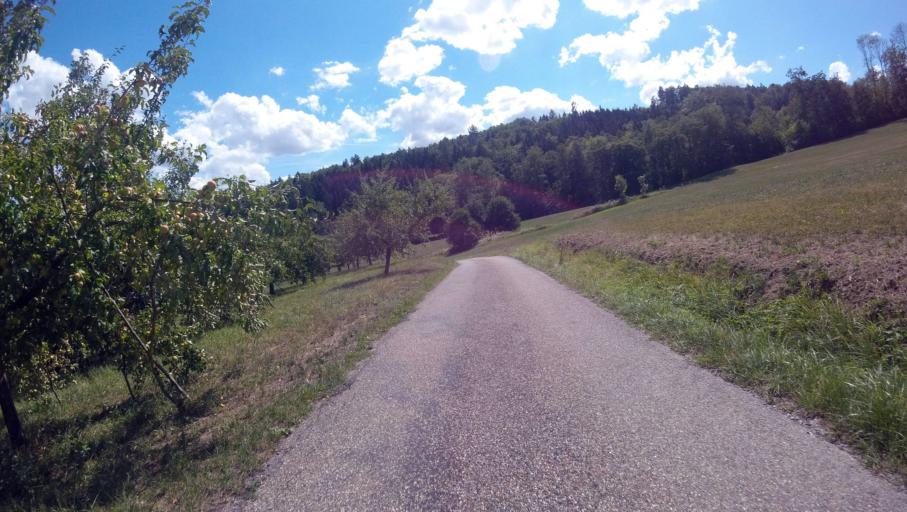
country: DE
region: Baden-Wuerttemberg
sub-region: Regierungsbezirk Stuttgart
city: Oppenweiler
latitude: 48.9963
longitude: 9.4427
